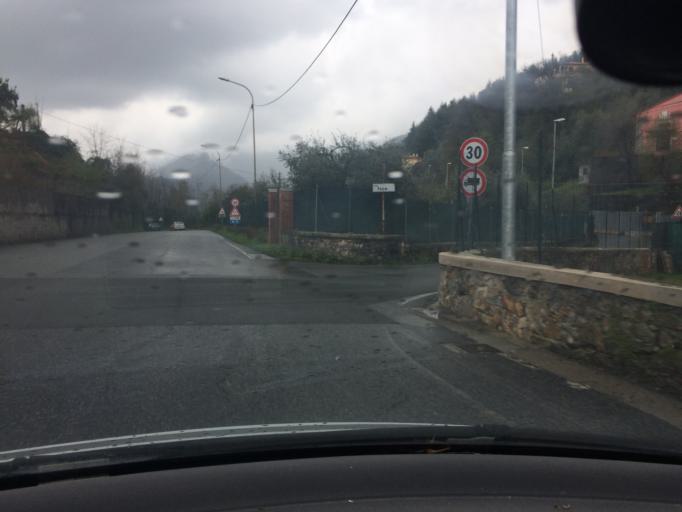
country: IT
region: Tuscany
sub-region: Provincia di Massa-Carrara
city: Massa
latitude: 44.0686
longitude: 10.1095
